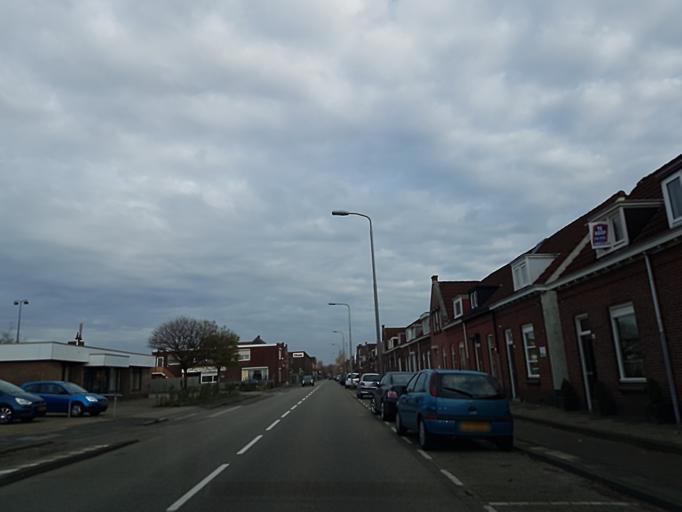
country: NL
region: North Brabant
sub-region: Roosendaal
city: Roosendaal
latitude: 51.5445
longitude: 4.4665
